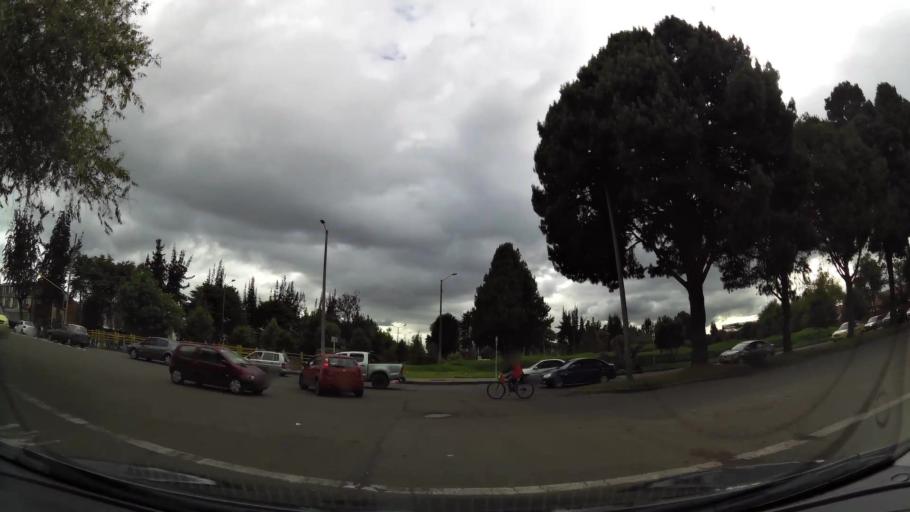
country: CO
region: Cundinamarca
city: Cota
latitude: 4.7214
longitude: -74.1107
